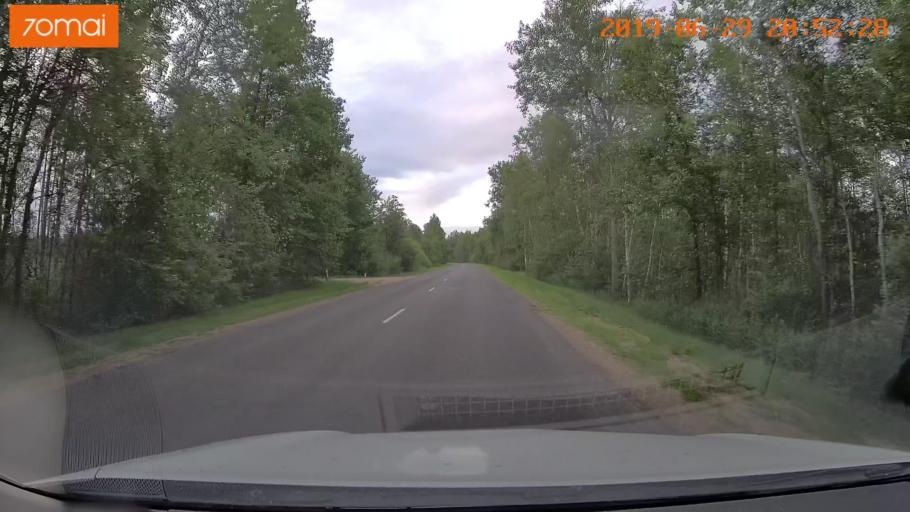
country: BY
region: Brest
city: Hantsavichy
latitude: 52.6997
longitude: 26.3632
